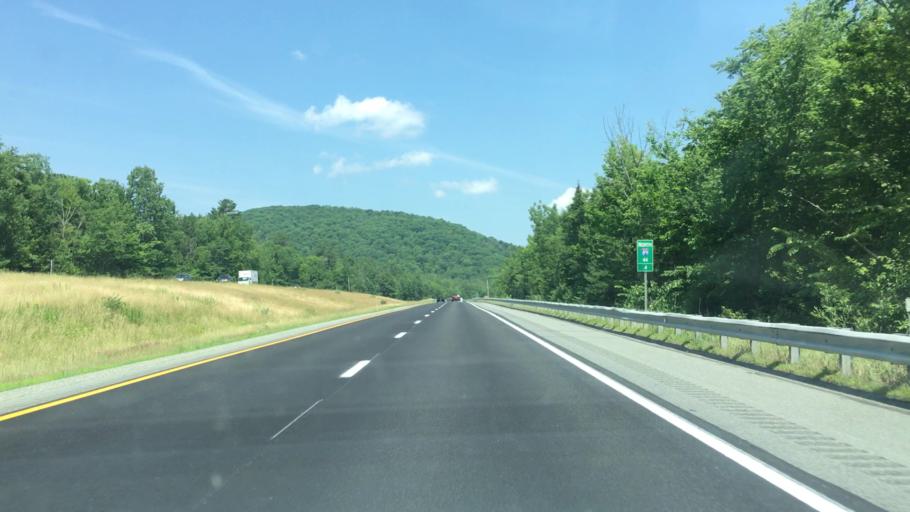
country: US
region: New Hampshire
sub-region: Sullivan County
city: Grantham
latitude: 43.5178
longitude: -72.1386
